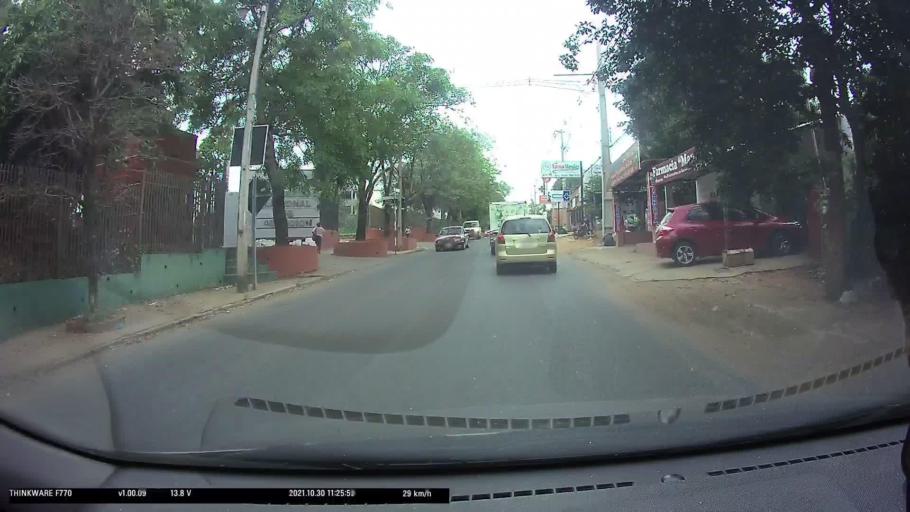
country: PY
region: Central
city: Fernando de la Mora
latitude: -25.3225
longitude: -57.5256
